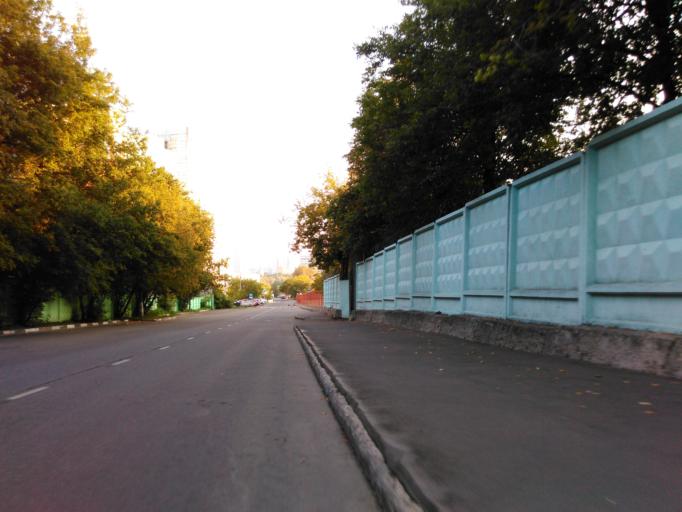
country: RU
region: Moskovskaya
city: Cheremushki
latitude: 55.6616
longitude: 37.5393
